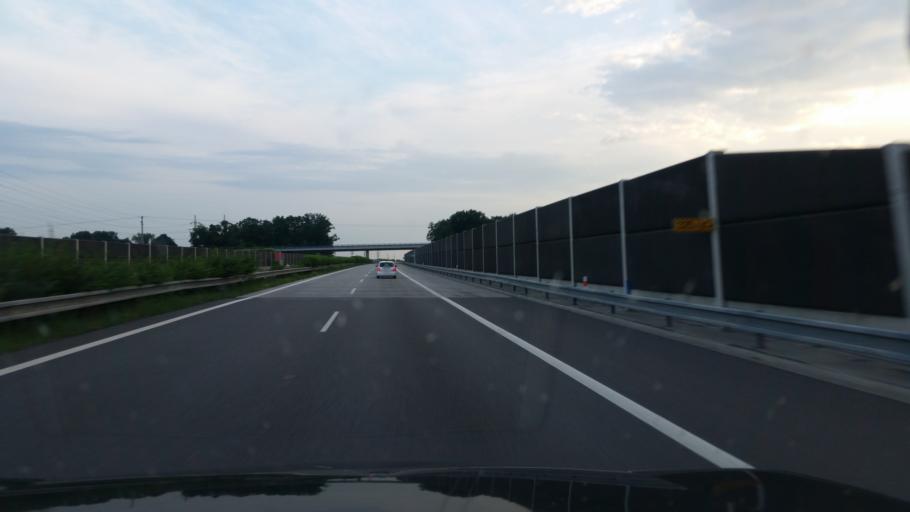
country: CZ
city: Fulnek
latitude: 49.6667
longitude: 17.9167
